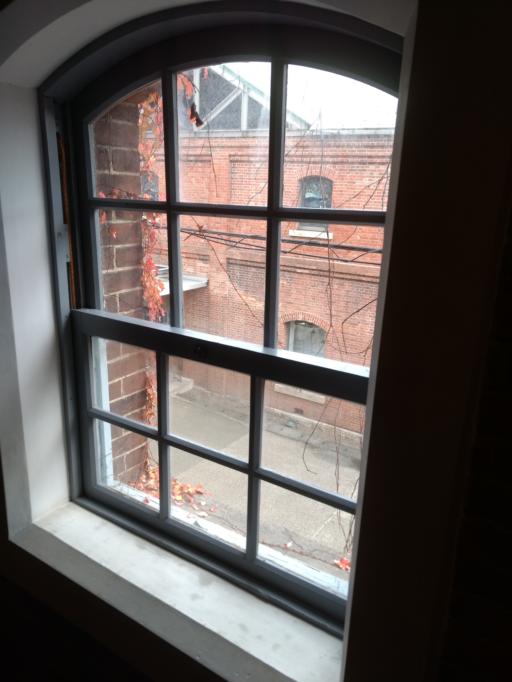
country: JP
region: Kyoto
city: Maizuru
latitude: 35.4746
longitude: 135.3853
